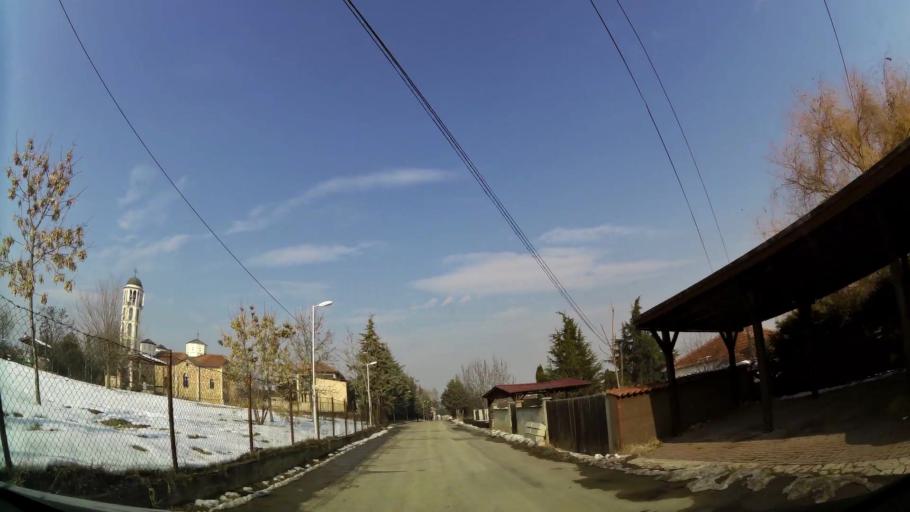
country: MK
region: Suto Orizari
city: Suto Orizare
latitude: 42.0286
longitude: 21.3787
